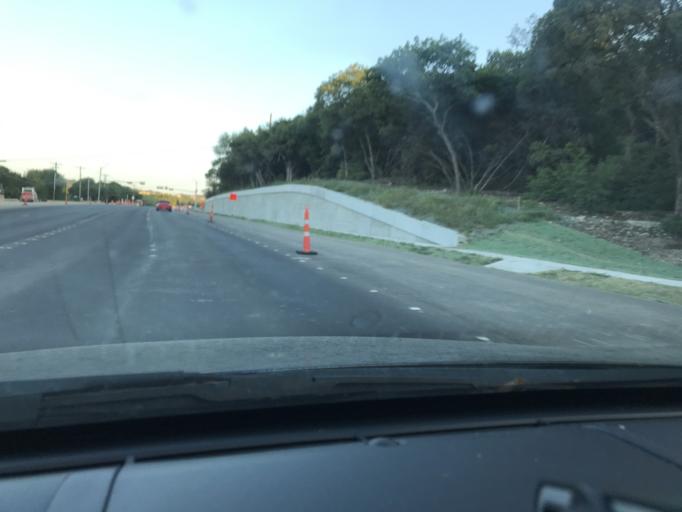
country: US
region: Texas
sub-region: Travis County
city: West Lake Hills
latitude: 30.2869
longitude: -97.8135
